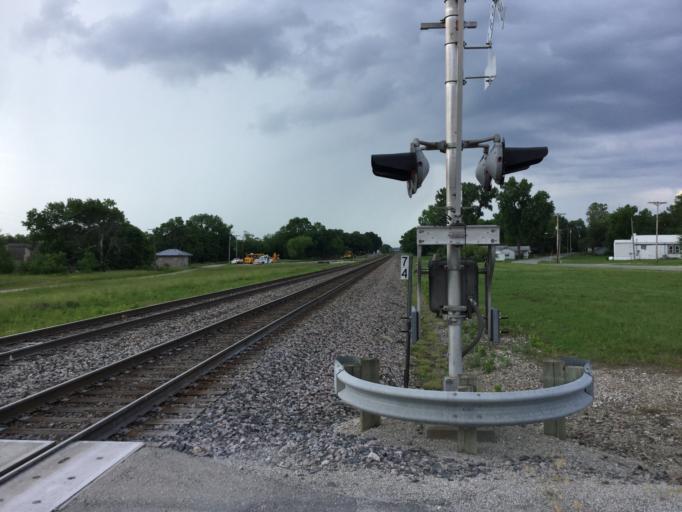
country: US
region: Kansas
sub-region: Linn County
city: Pleasanton
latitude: 38.1753
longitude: -94.7089
